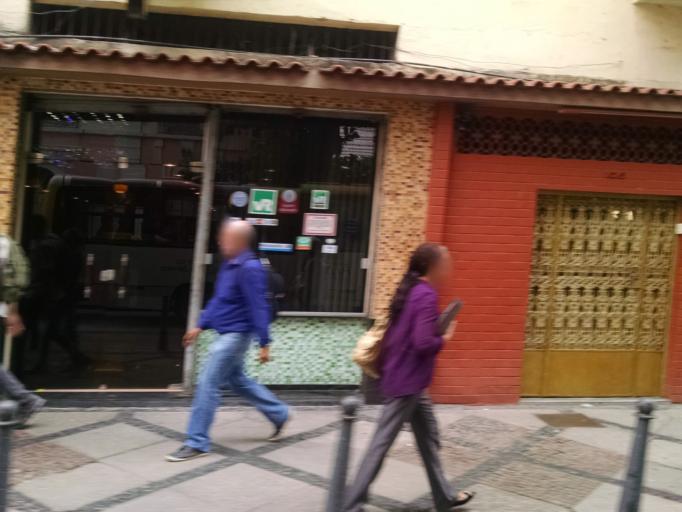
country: BR
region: Rio de Janeiro
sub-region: Rio De Janeiro
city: Rio de Janeiro
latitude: -22.9117
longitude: -43.1824
